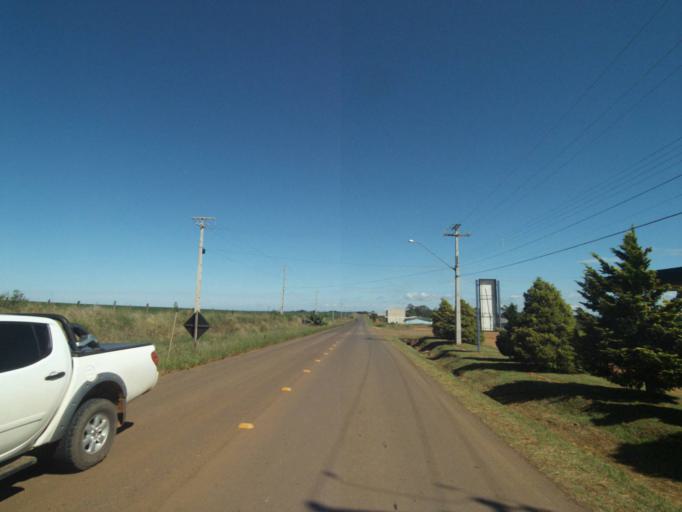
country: BR
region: Parana
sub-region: Pinhao
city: Pinhao
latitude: -25.8322
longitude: -52.0330
